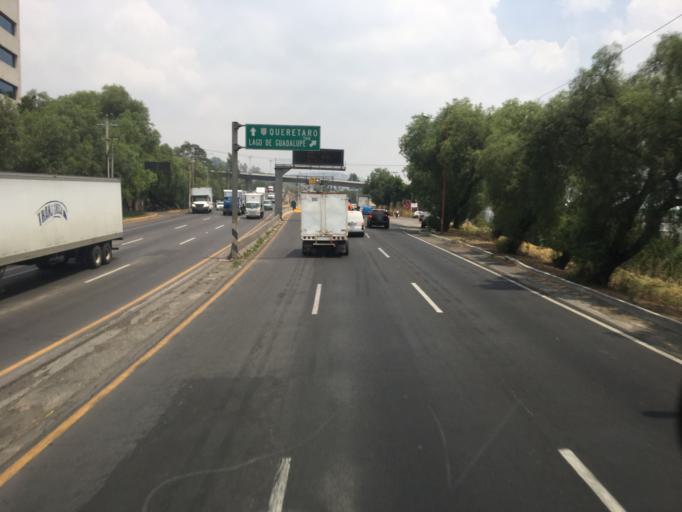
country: MX
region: Mexico
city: Tlalnepantla
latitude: 19.5672
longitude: -99.2067
